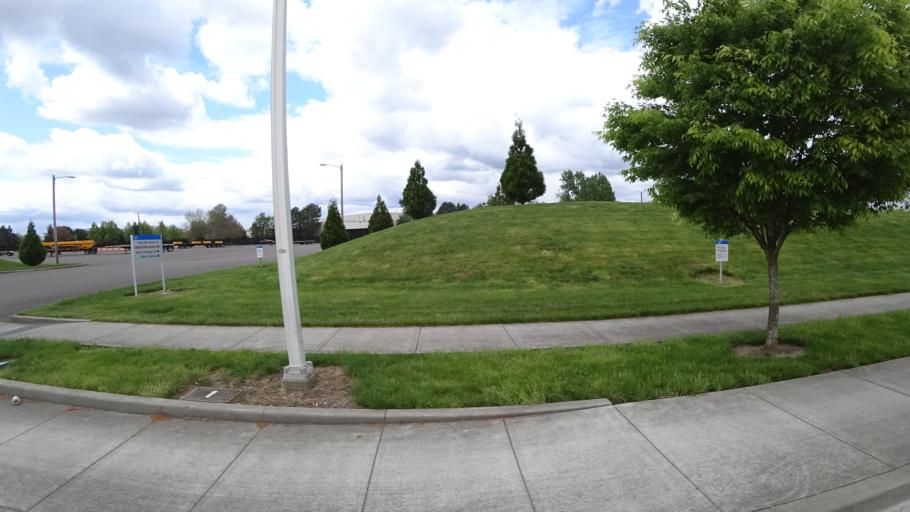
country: US
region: Oregon
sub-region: Washington County
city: Rockcreek
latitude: 45.5426
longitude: -122.9025
